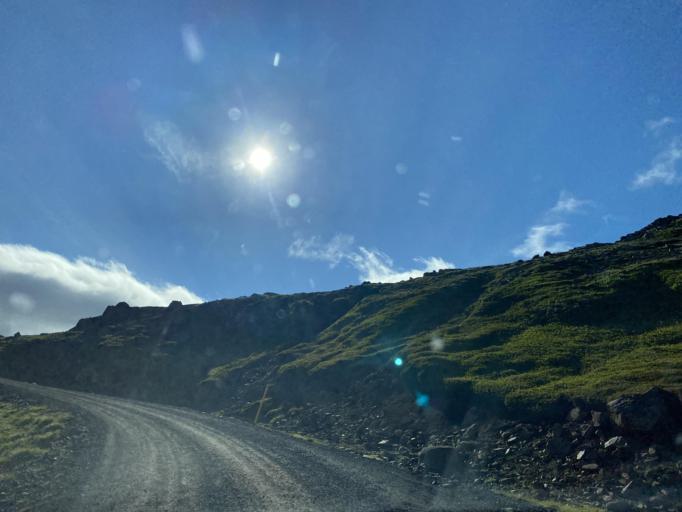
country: IS
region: East
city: Eskifjoerdur
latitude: 65.1806
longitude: -14.0900
